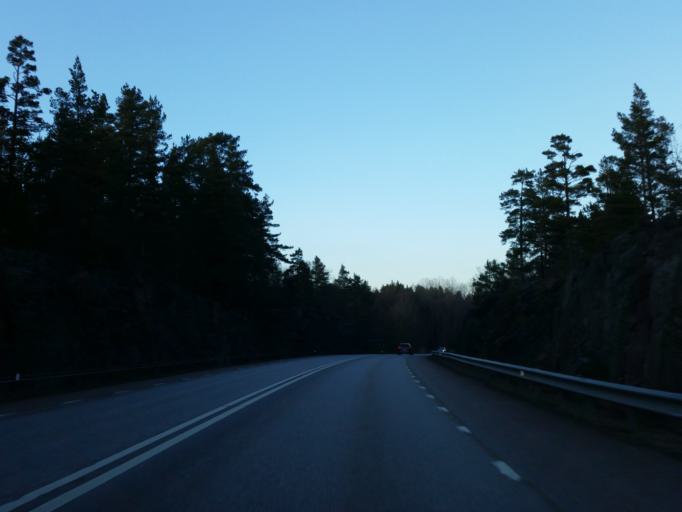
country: SE
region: Kalmar
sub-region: Oskarshamns Kommun
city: Oskarshamn
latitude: 57.4388
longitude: 16.4914
